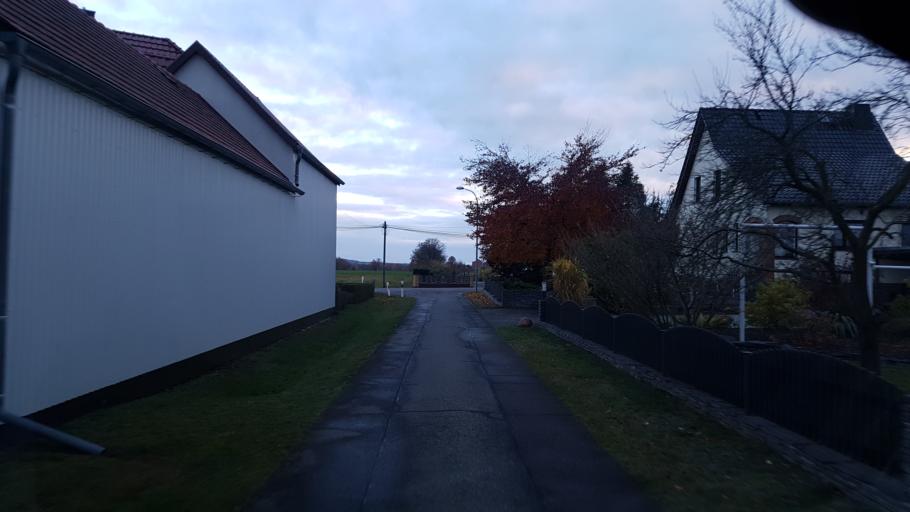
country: DE
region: Brandenburg
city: Schraden
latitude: 51.4274
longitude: 13.6993
